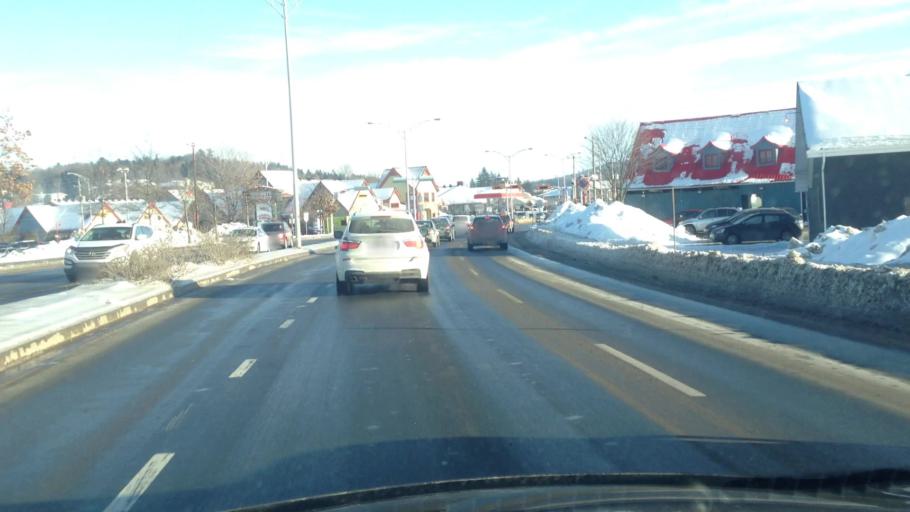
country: CA
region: Quebec
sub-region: Laurentides
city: Saint-Sauveur
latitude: 45.8922
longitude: -74.1530
